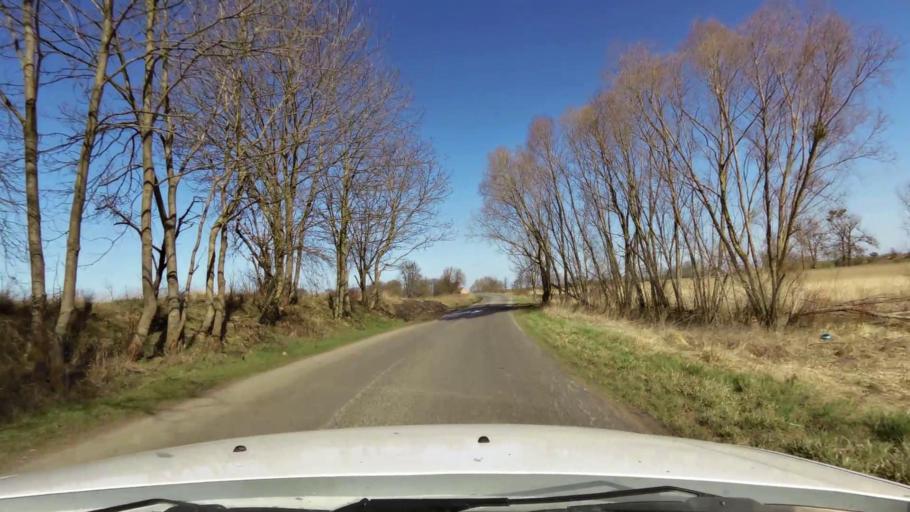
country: PL
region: West Pomeranian Voivodeship
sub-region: Powiat gryfinski
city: Cedynia
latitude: 52.8788
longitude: 14.2860
